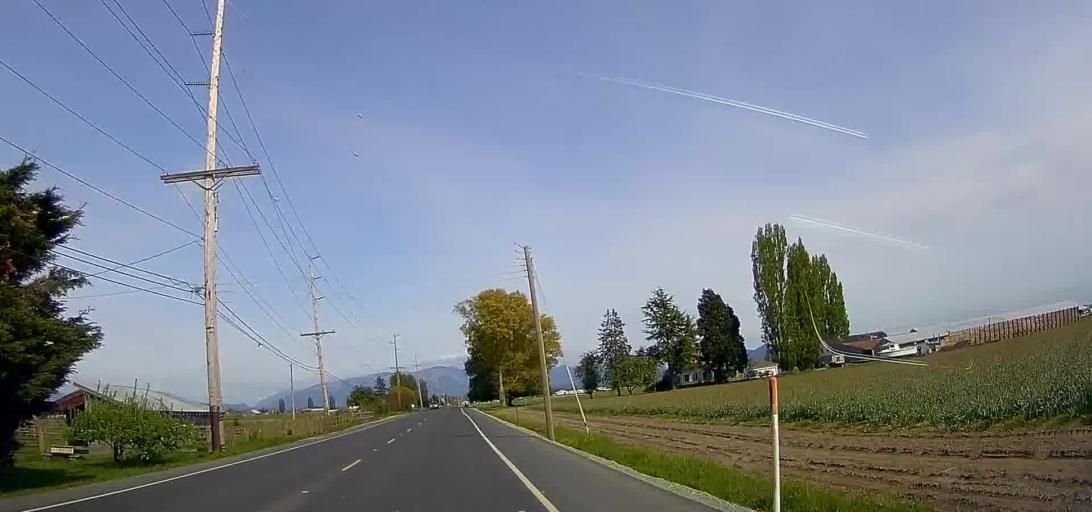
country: US
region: Washington
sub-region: Skagit County
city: Mount Vernon
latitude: 48.4209
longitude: -122.4665
